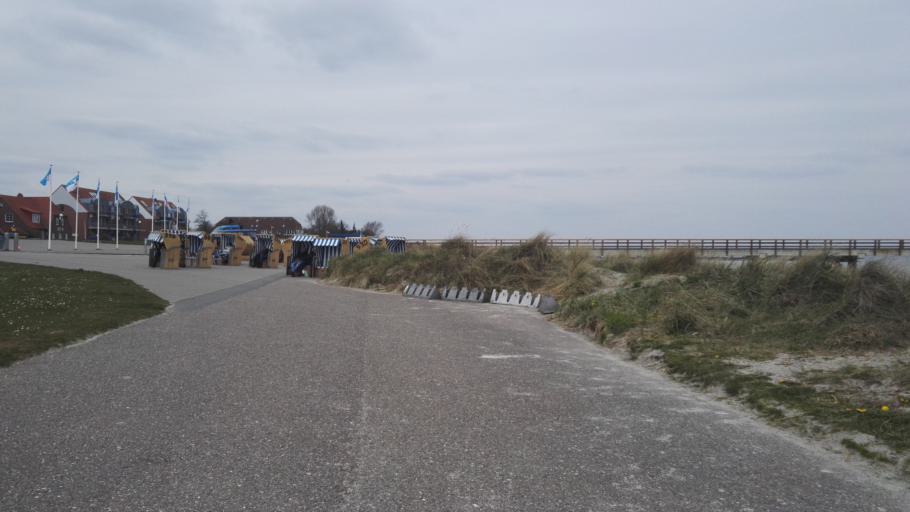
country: DE
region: Schleswig-Holstein
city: Krummbek
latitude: 54.4143
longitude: 10.4151
